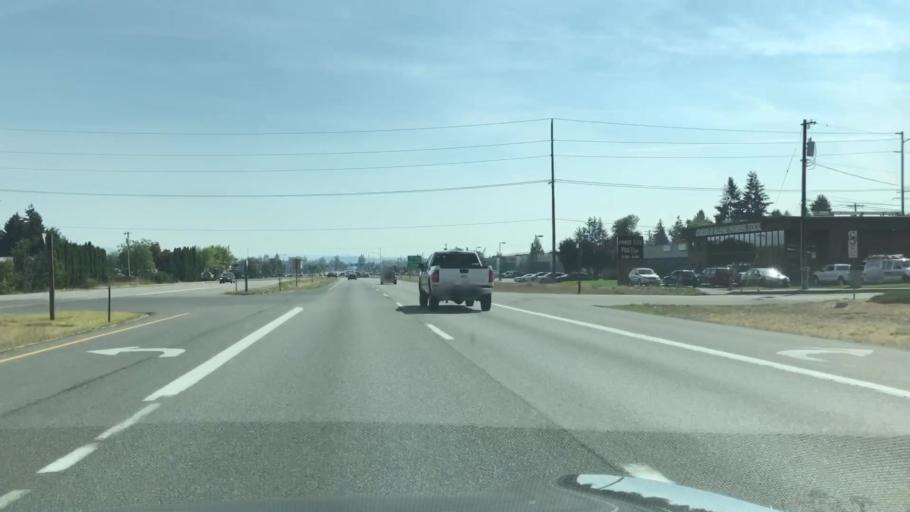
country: US
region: Idaho
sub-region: Kootenai County
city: Coeur d'Alene
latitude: 47.7053
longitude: -116.7917
